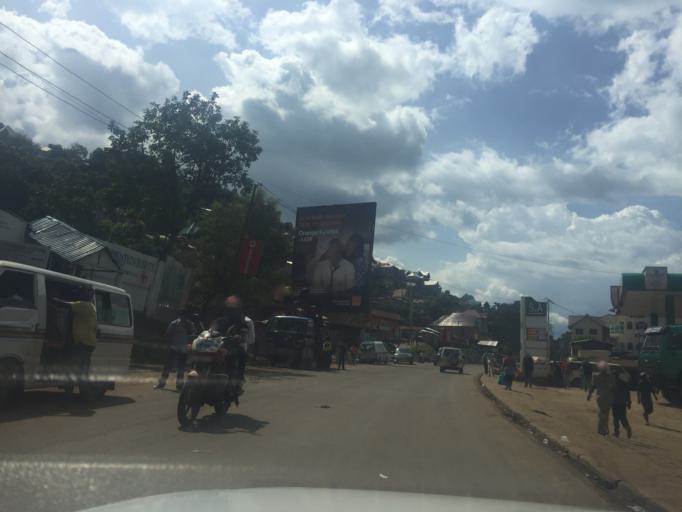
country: CD
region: South Kivu
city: Bukavu
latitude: -2.4887
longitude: 28.8476
